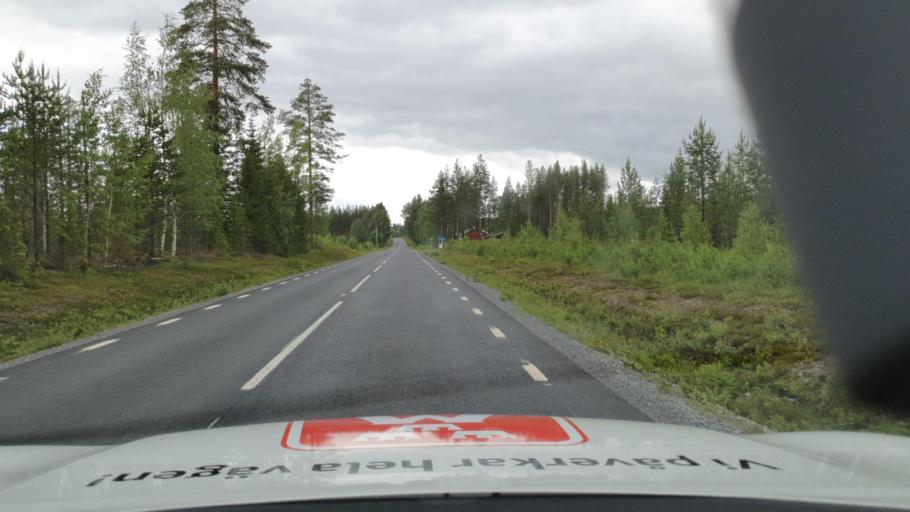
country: SE
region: Vaesterbotten
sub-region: Dorotea Kommun
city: Dorotea
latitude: 64.2116
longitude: 16.5544
